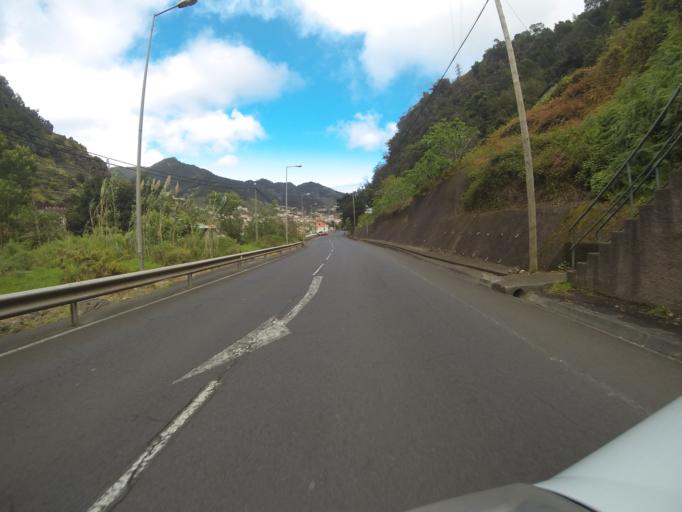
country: PT
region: Madeira
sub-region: Machico
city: Machico
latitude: 32.7320
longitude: -16.7802
